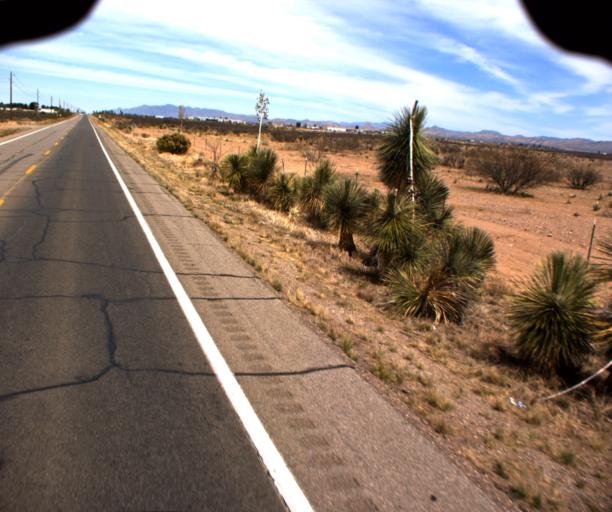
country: US
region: Arizona
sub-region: Cochise County
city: Pirtleville
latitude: 31.3805
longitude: -109.5793
